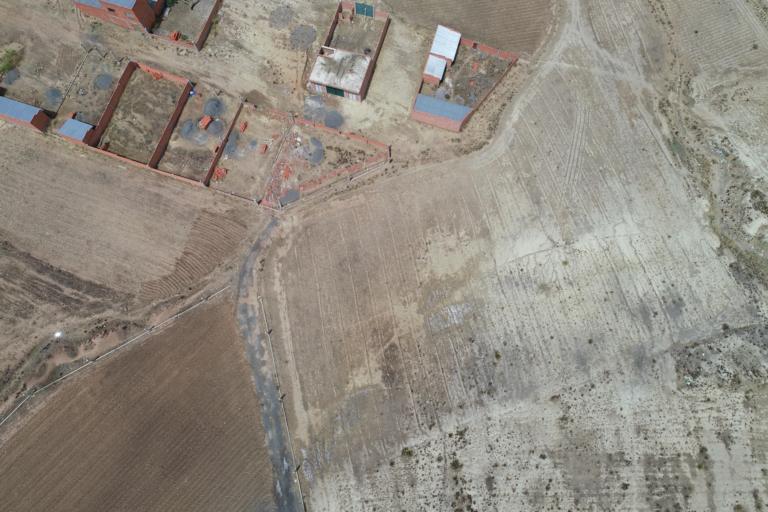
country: BO
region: La Paz
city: Achacachi
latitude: -16.0548
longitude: -68.6778
